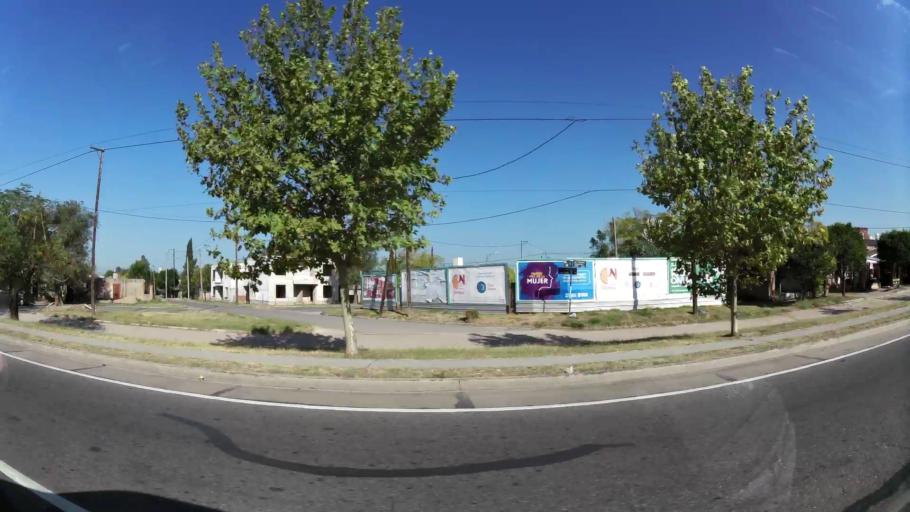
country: AR
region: Cordoba
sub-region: Departamento de Capital
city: Cordoba
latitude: -31.4773
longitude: -64.2366
